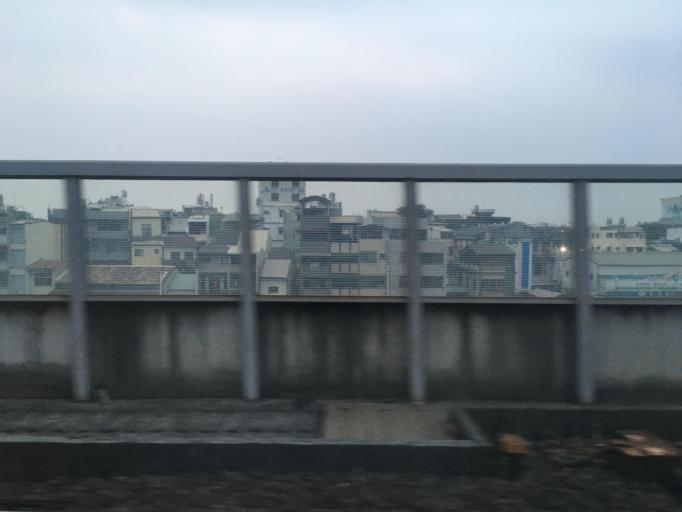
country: TW
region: Taiwan
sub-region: Pingtung
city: Pingtung
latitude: 22.6694
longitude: 120.4829
